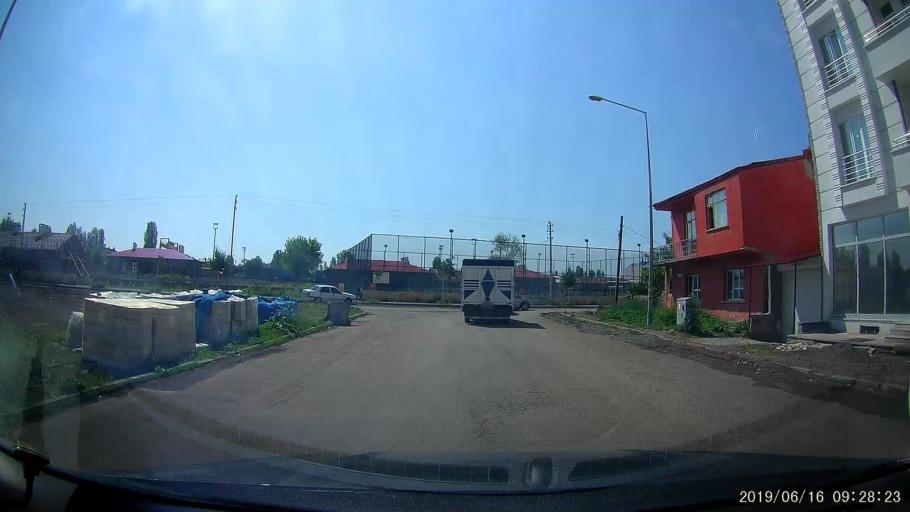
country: TR
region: Kars
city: Kars
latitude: 40.6036
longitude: 43.1038
